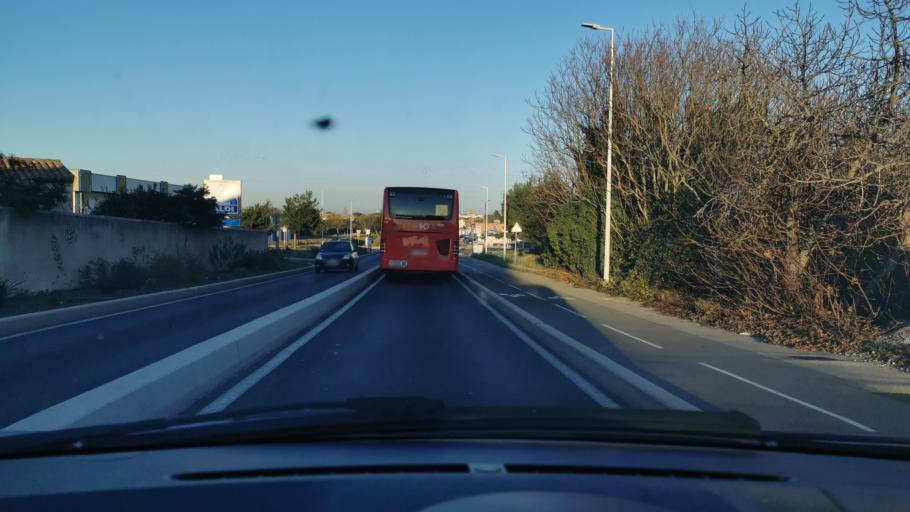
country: FR
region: Languedoc-Roussillon
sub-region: Departement de l'Herault
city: Frontignan
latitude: 43.4369
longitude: 3.7404
